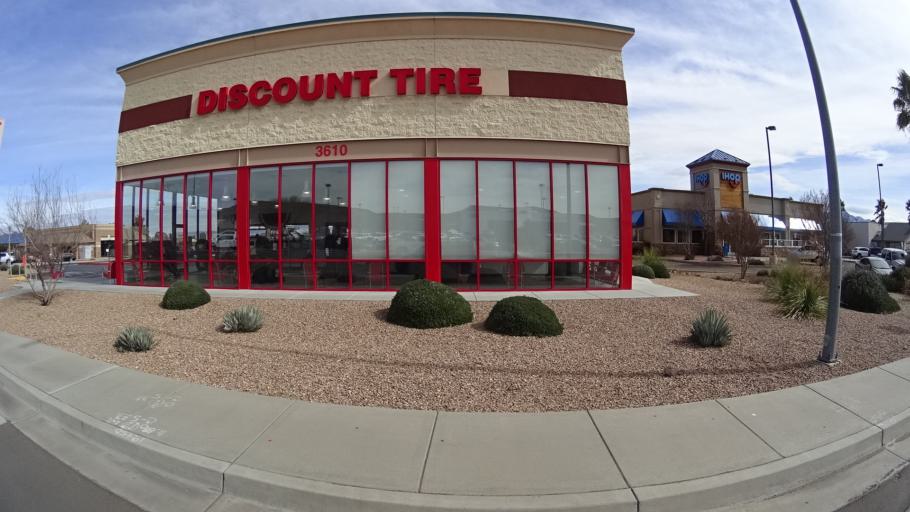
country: US
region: Arizona
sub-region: Mohave County
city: New Kingman-Butler
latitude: 35.2273
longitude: -114.0365
